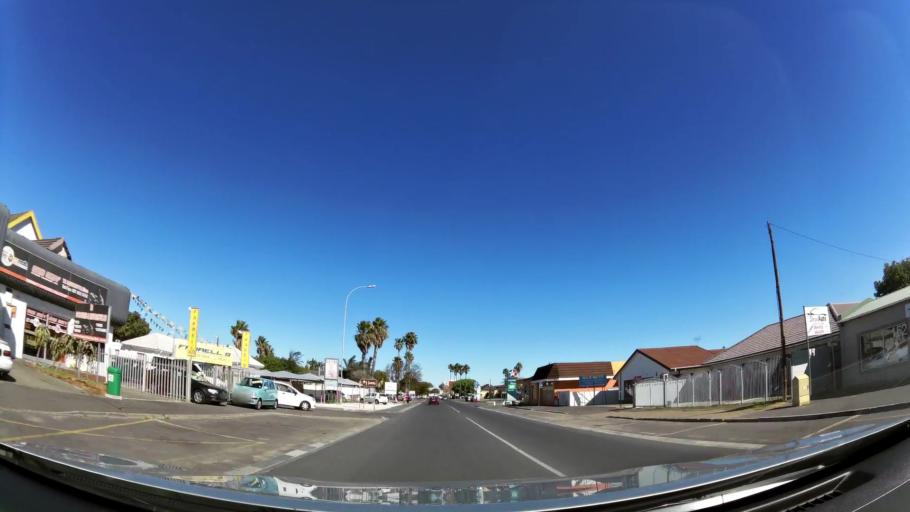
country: ZA
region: Western Cape
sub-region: Cape Winelands District Municipality
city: Stellenbosch
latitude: -34.1098
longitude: 18.8362
